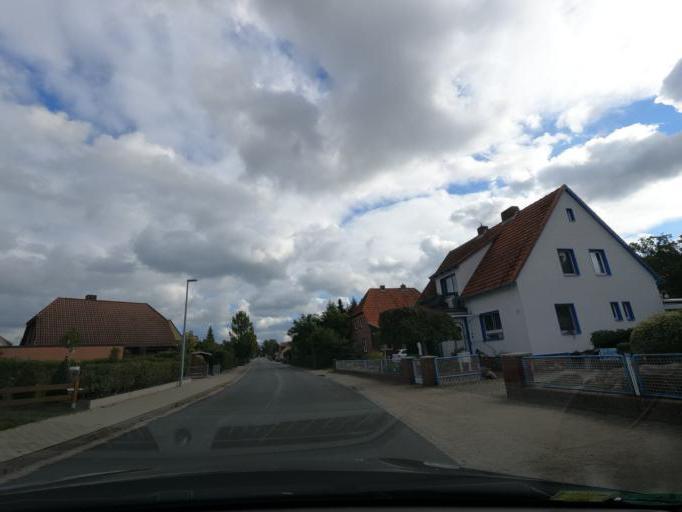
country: DE
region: Lower Saxony
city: Klein Schwulper
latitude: 52.3485
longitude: 10.4388
